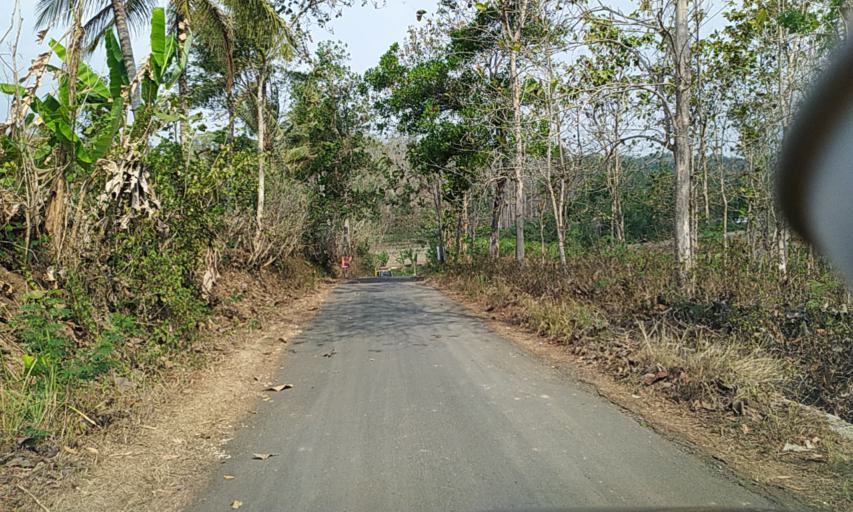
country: ID
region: Central Java
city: Karanggintung
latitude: -7.4677
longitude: 108.8850
